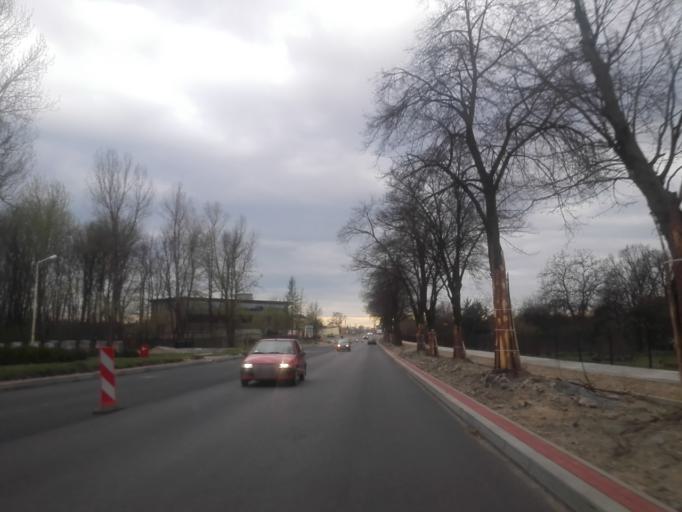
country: PL
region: Silesian Voivodeship
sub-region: Czestochowa
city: Czestochowa
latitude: 50.8353
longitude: 19.1529
